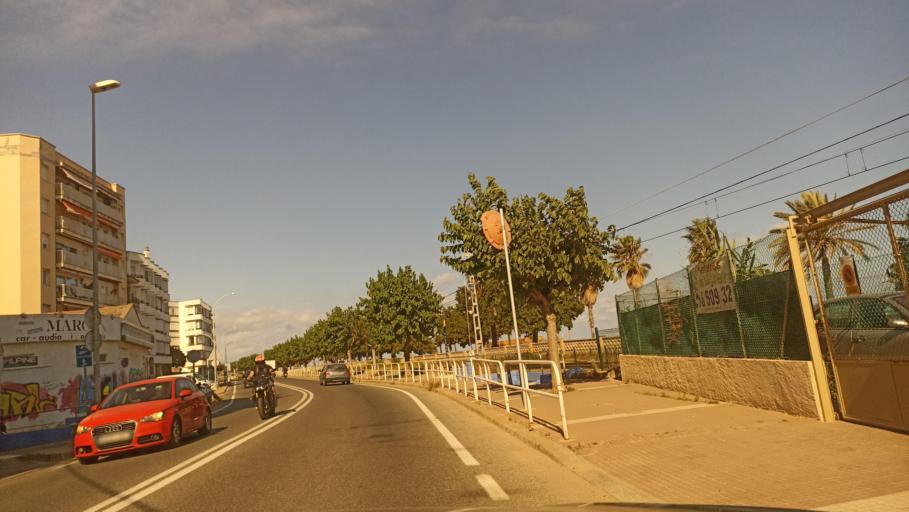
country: ES
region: Catalonia
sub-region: Provincia de Barcelona
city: Canet de Mar
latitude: 41.5874
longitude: 2.5834
